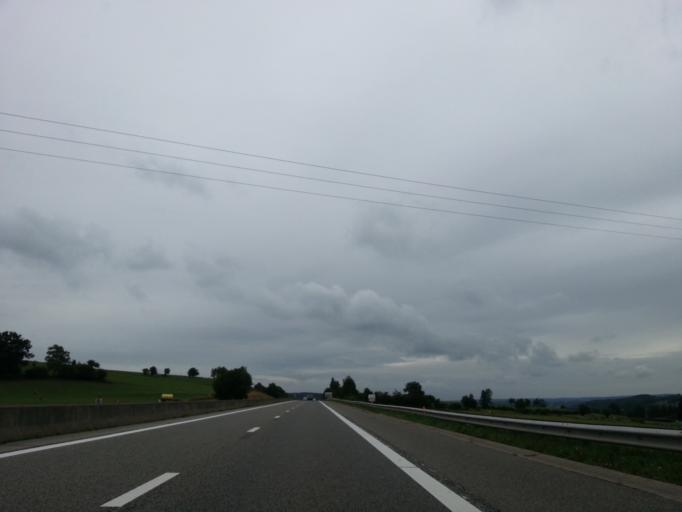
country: BE
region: Wallonia
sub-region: Province de Liege
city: Malmedy
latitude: 50.3589
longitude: 6.0505
